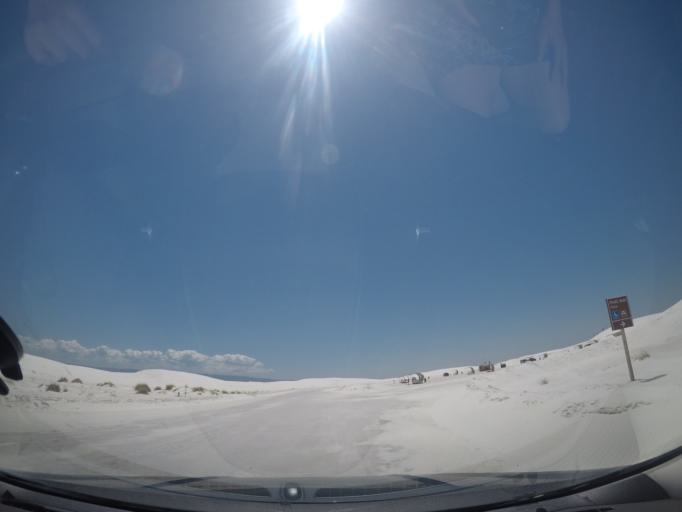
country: US
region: New Mexico
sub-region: Otero County
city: Holloman Air Force Base
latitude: 32.8149
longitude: -106.2675
